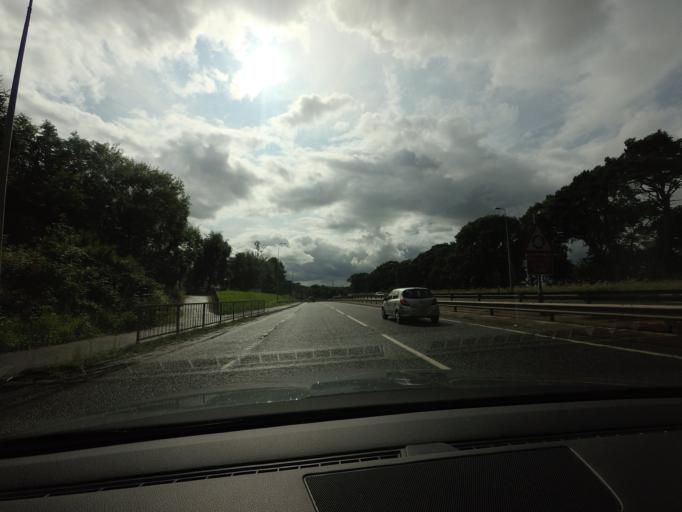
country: GB
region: Scotland
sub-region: Highland
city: Inverness
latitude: 57.4828
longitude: -4.1865
